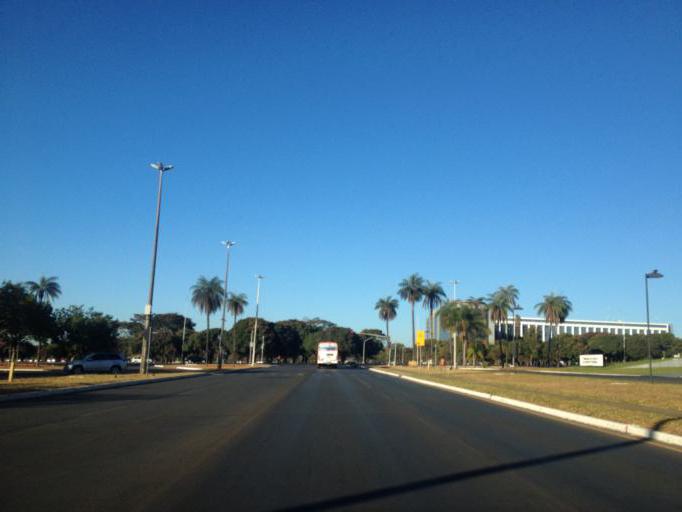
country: BR
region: Federal District
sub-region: Brasilia
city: Brasilia
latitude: -15.7841
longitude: -47.9059
